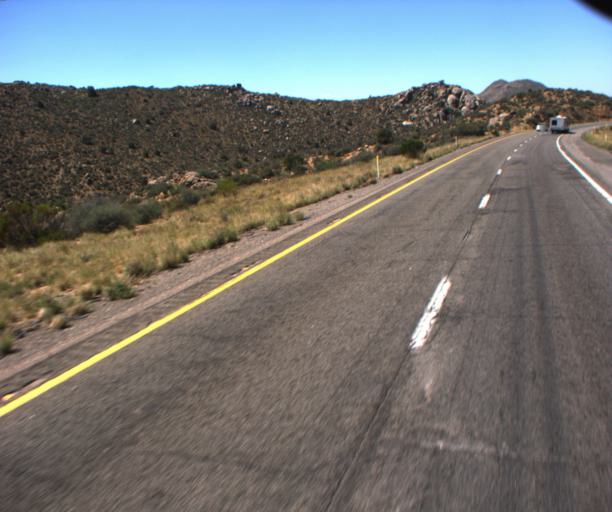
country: US
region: Arizona
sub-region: Mohave County
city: Peach Springs
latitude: 35.1755
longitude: -113.5007
